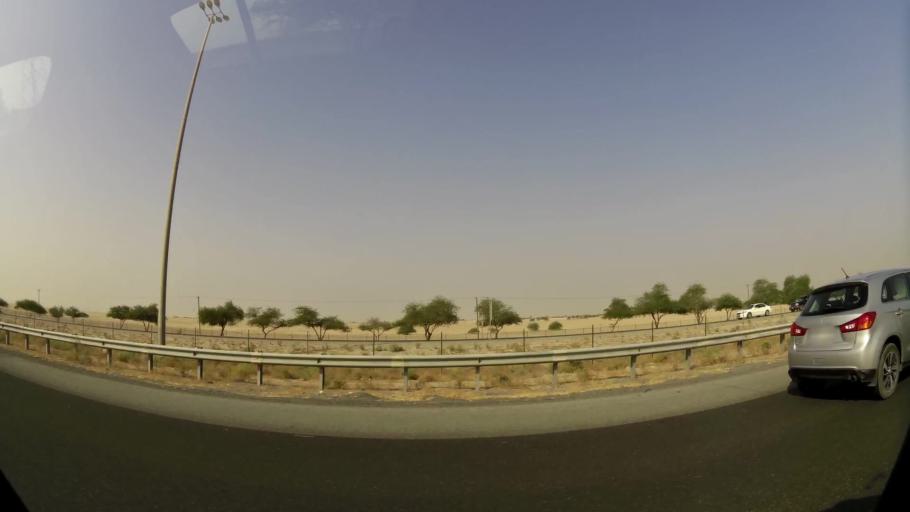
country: KW
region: Al Asimah
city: Ar Rabiyah
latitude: 29.2280
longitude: 47.8852
